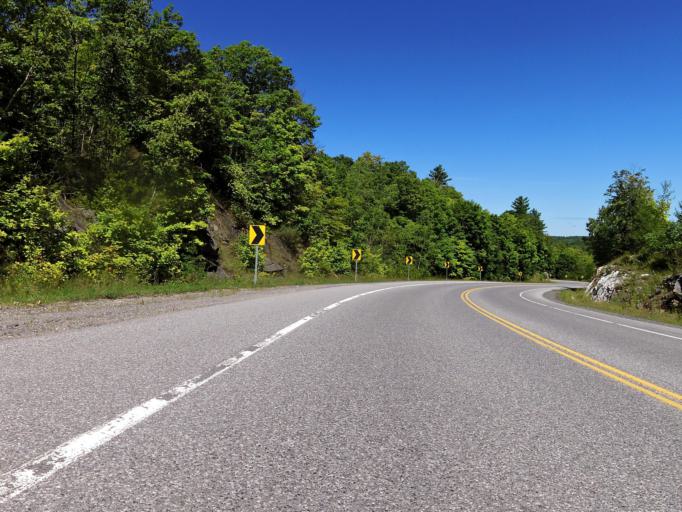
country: CA
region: Ontario
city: Arnprior
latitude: 45.1559
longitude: -76.5186
